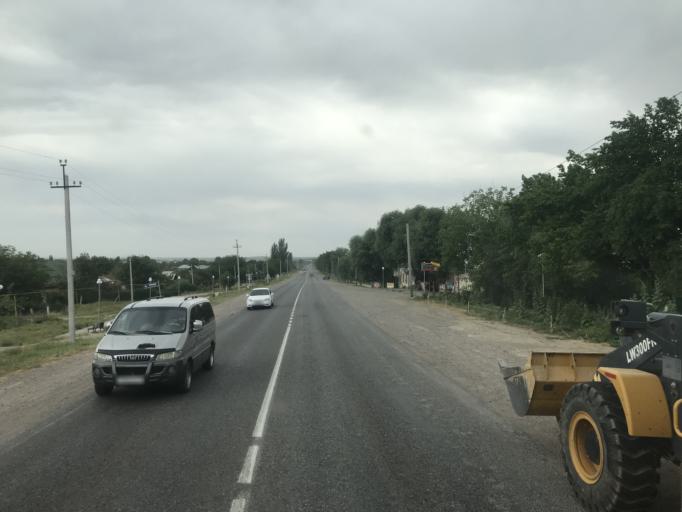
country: UZ
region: Toshkent
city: Salor
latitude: 41.4939
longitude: 69.3213
